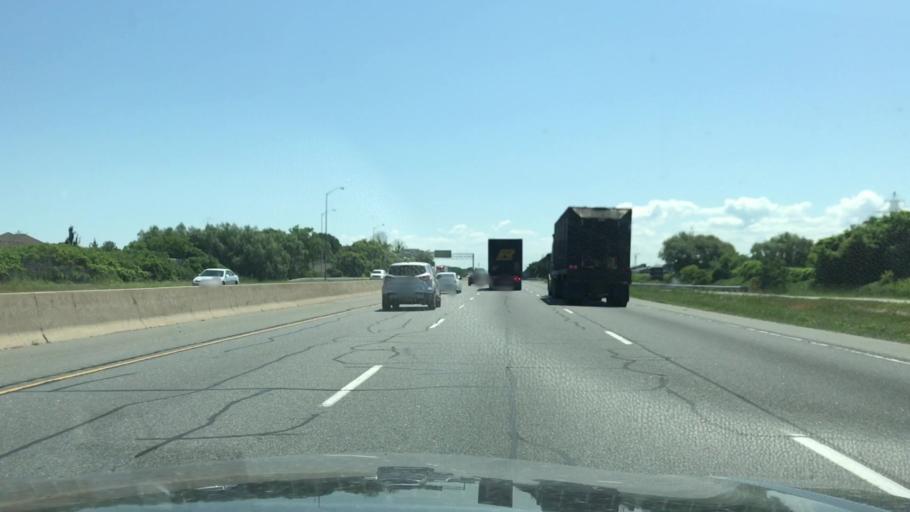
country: CA
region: Ontario
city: Oakville
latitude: 43.1965
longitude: -79.5502
